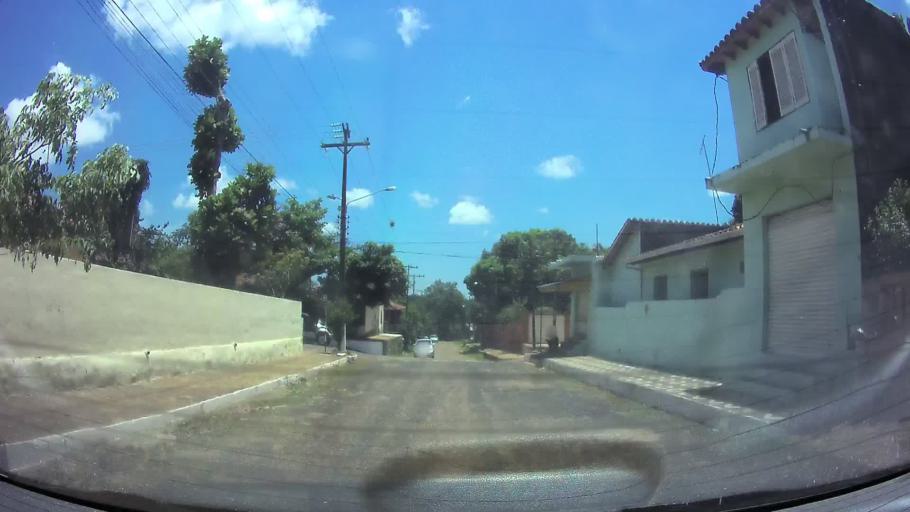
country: PY
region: Central
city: San Lorenzo
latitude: -25.2585
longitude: -57.4850
